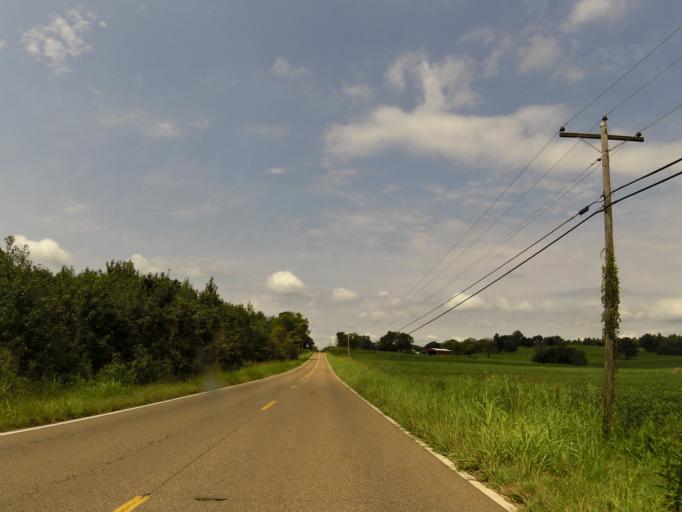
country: US
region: Tennessee
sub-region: Decatur County
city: Decaturville
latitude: 35.5806
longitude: -88.1027
